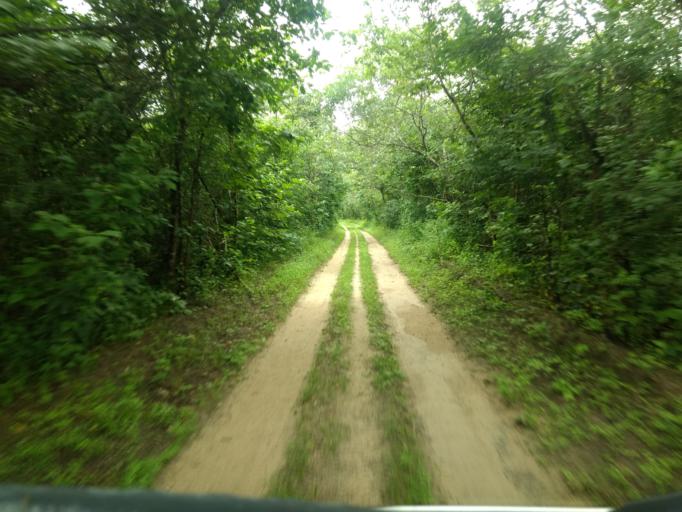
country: BR
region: Ceara
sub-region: Crateus
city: Crateus
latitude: -5.1502
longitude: -40.9194
